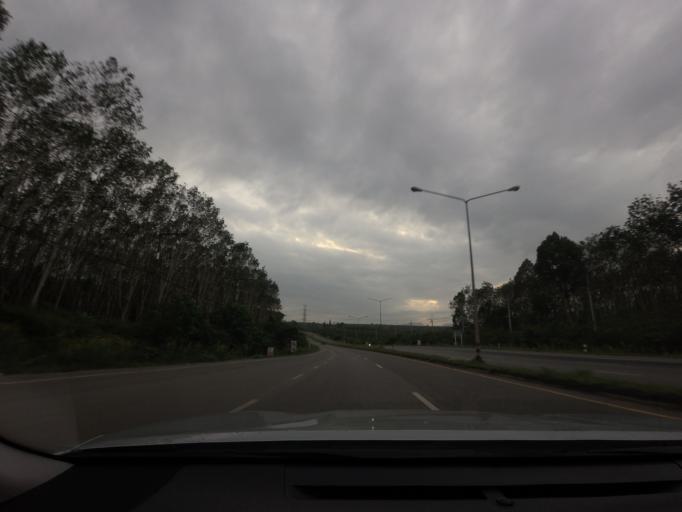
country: TH
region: Surat Thani
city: Phunphin
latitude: 9.0399
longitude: 99.1072
